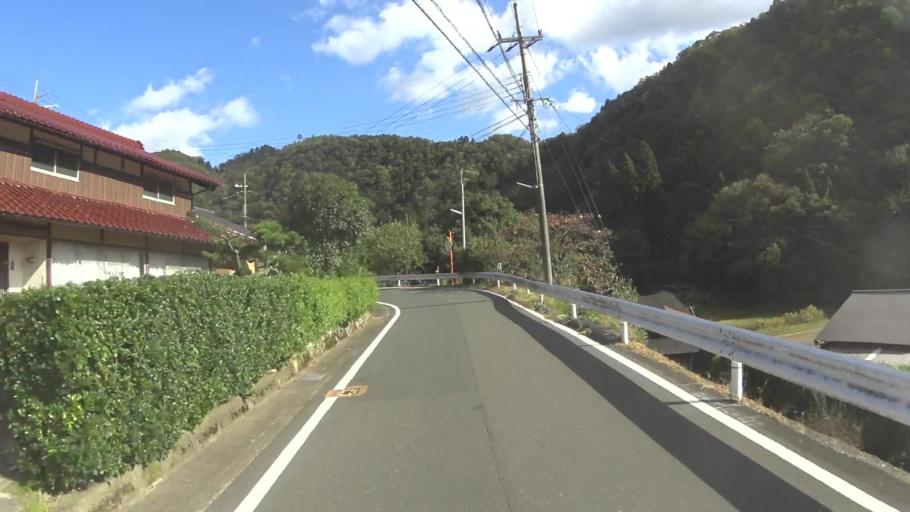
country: JP
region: Kyoto
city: Maizuru
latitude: 35.5318
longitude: 135.4372
